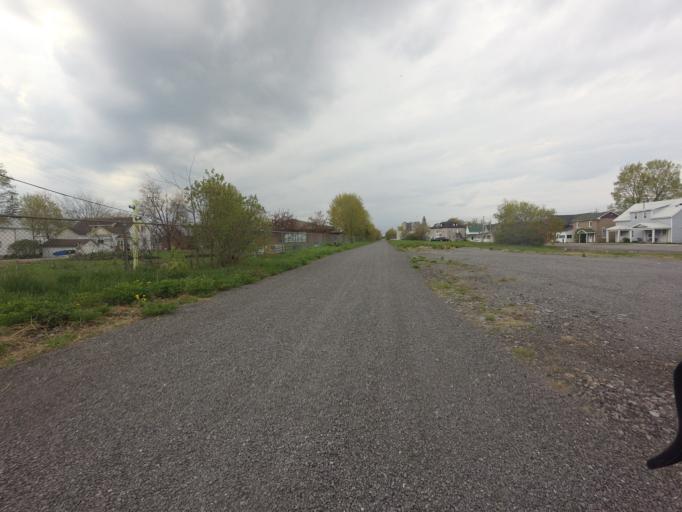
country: CA
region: Ontario
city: Carleton Place
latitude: 45.2239
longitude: -76.1919
